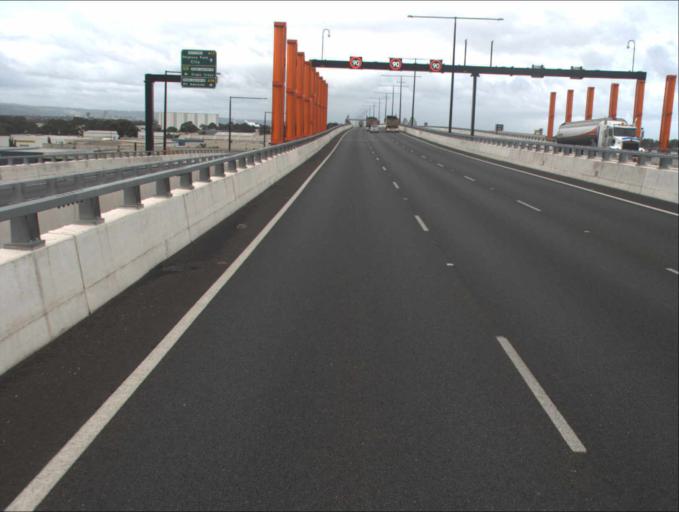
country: AU
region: South Australia
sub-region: Charles Sturt
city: Woodville North
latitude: -34.8459
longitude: 138.5645
